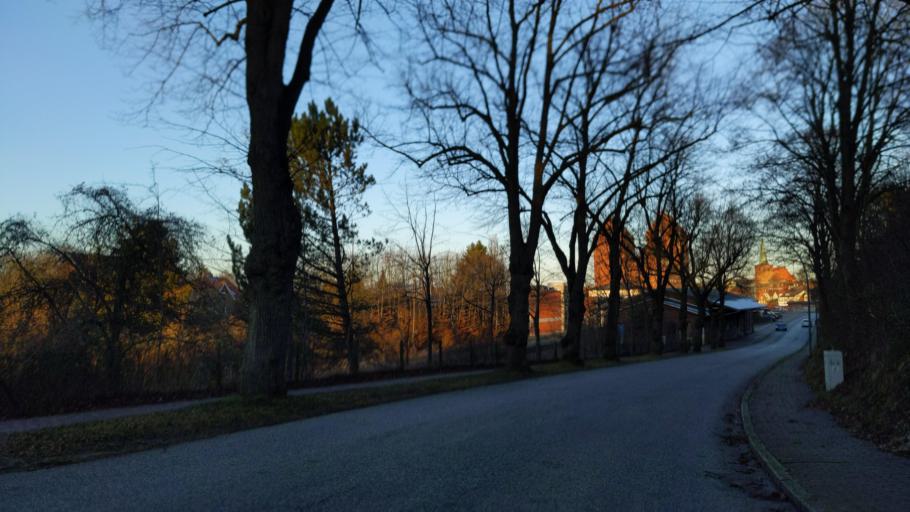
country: DE
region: Schleswig-Holstein
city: Neustadt in Holstein
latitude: 54.1027
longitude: 10.8064
